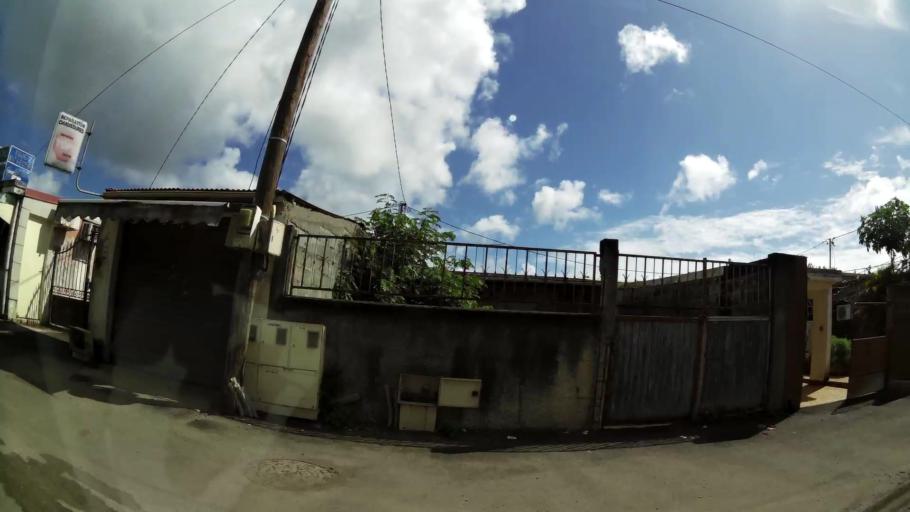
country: GP
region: Guadeloupe
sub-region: Guadeloupe
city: Pointe-a-Pitre
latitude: 16.2562
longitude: -61.5270
